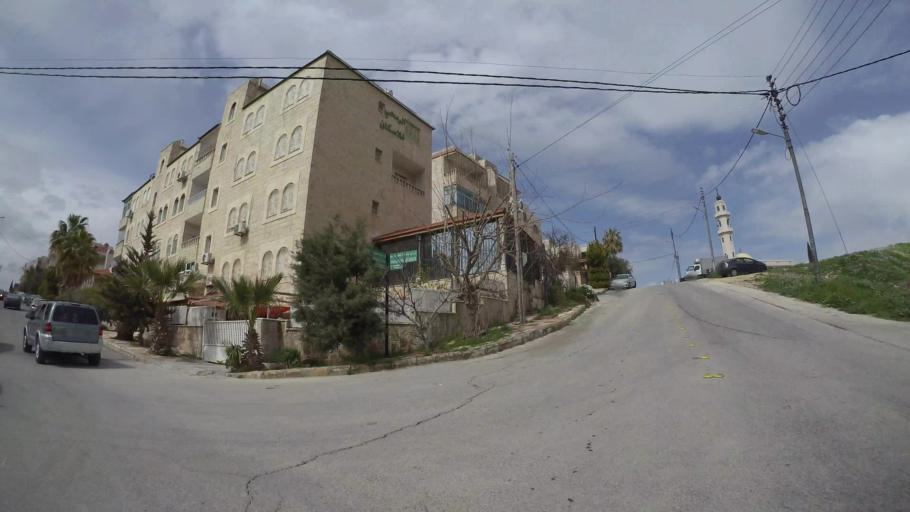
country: JO
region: Amman
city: Amman
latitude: 31.9915
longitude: 35.9405
